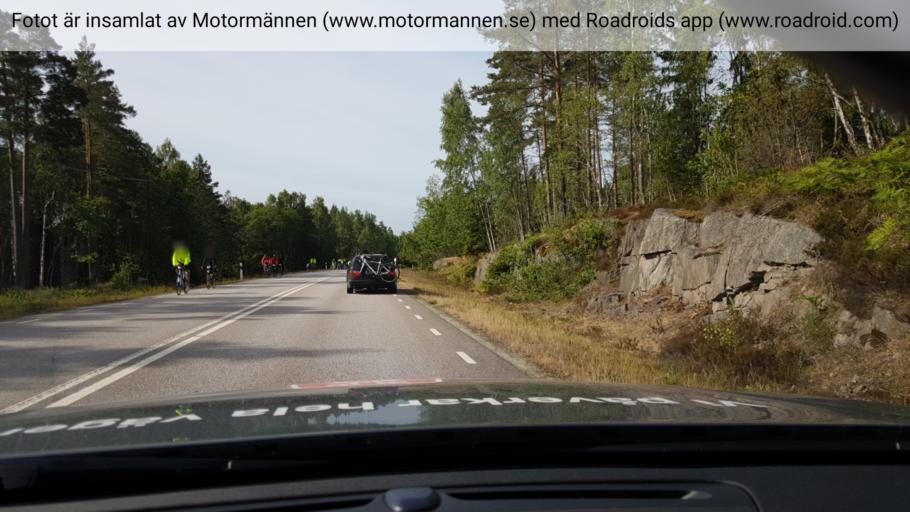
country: SE
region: Vaestra Goetaland
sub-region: Karlsborgs Kommun
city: Karlsborg
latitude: 58.6096
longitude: 14.5324
